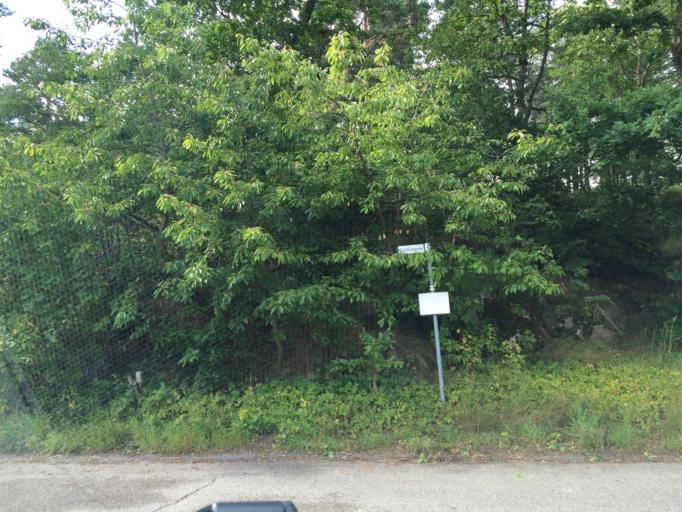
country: SE
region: Vaestra Goetaland
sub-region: Trollhattan
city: Trollhattan
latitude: 58.2872
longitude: 12.2673
